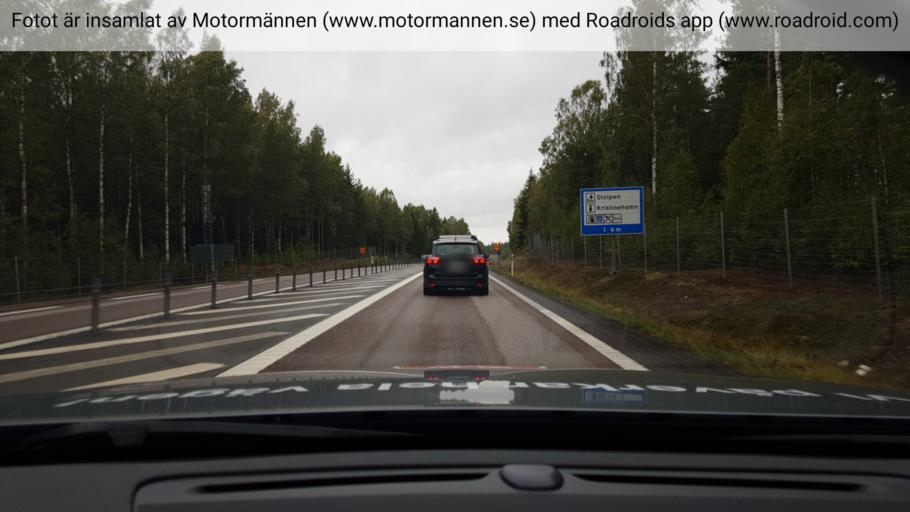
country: SE
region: Vaermland
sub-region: Kristinehamns Kommun
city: Kristinehamn
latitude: 59.3639
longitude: 14.0255
